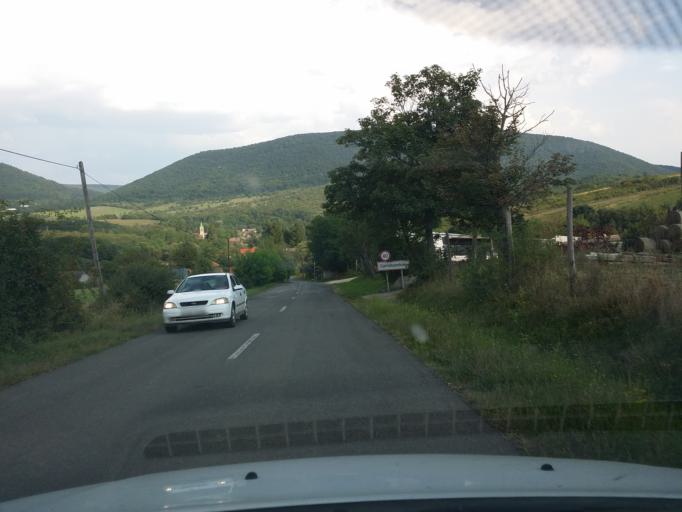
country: HU
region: Nograd
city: Bujak
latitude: 47.9422
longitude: 19.5726
